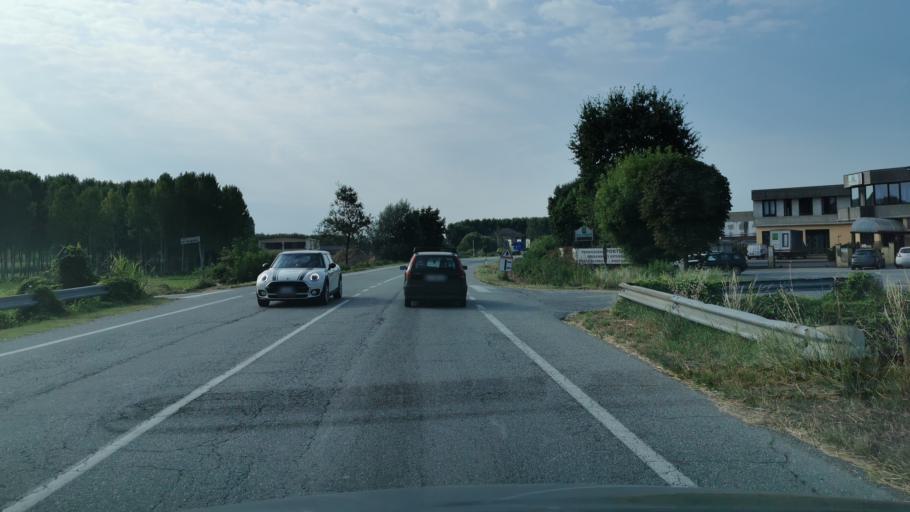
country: IT
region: Piedmont
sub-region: Provincia di Torino
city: Cercenasco
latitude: 44.8611
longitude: 7.5106
